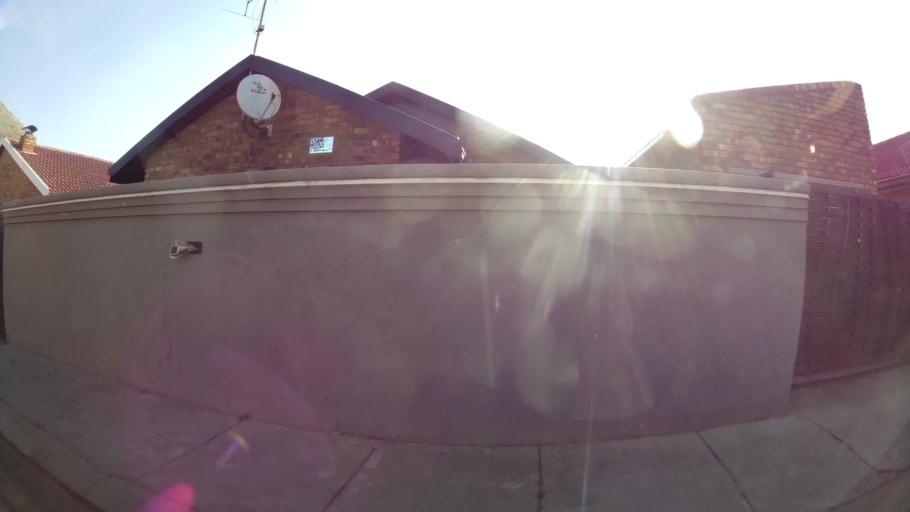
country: ZA
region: Gauteng
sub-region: City of Johannesburg Metropolitan Municipality
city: Soweto
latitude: -26.2704
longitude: 27.9149
